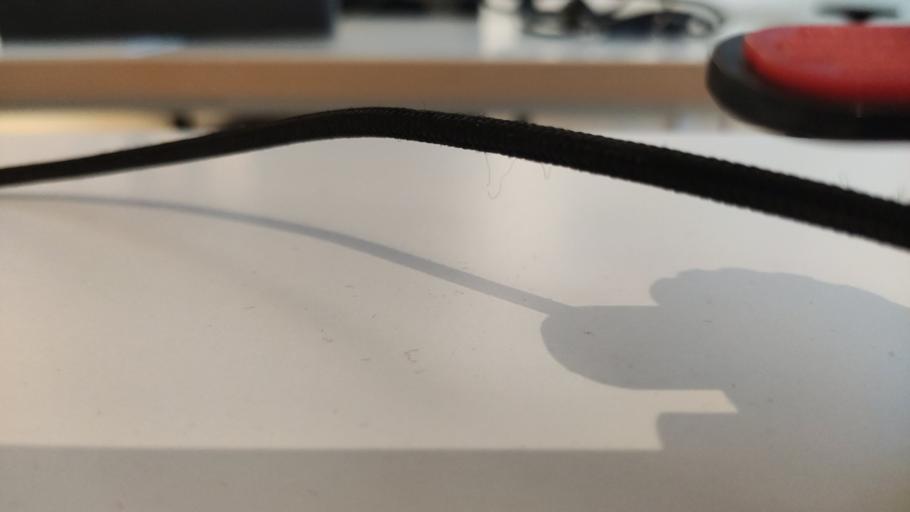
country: RU
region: Moskovskaya
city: Novopetrovskoye
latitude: 55.8740
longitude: 36.4040
